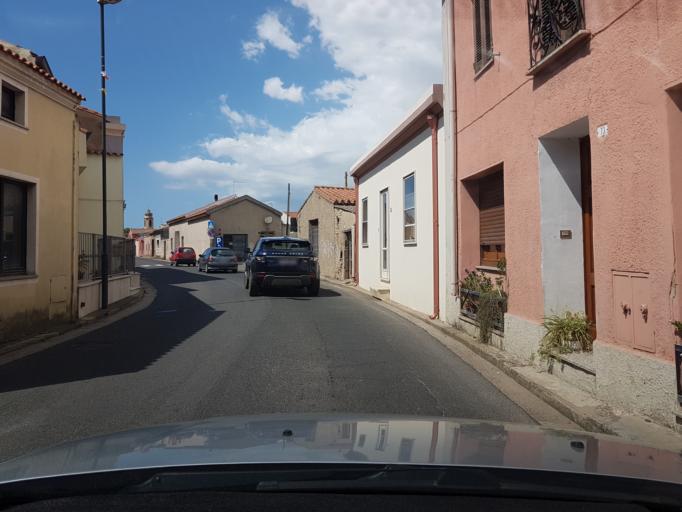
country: IT
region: Sardinia
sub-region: Provincia di Oristano
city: Riola Sardo
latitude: 39.9939
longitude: 8.5412
